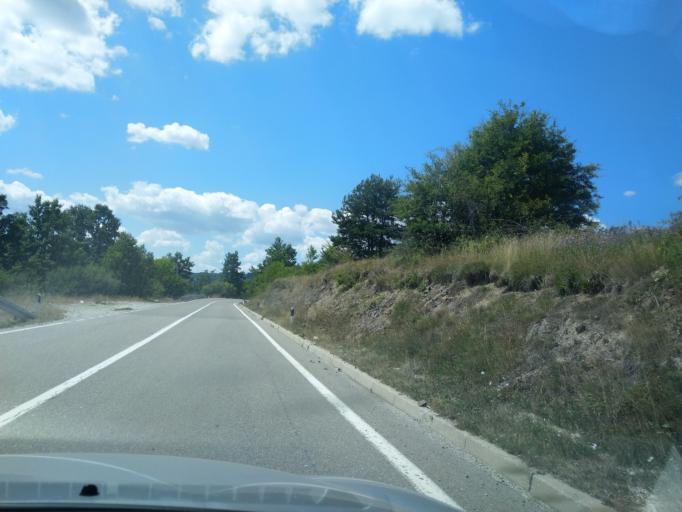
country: RS
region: Central Serbia
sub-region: Zlatiborski Okrug
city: Sjenica
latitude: 43.3064
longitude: 19.9269
